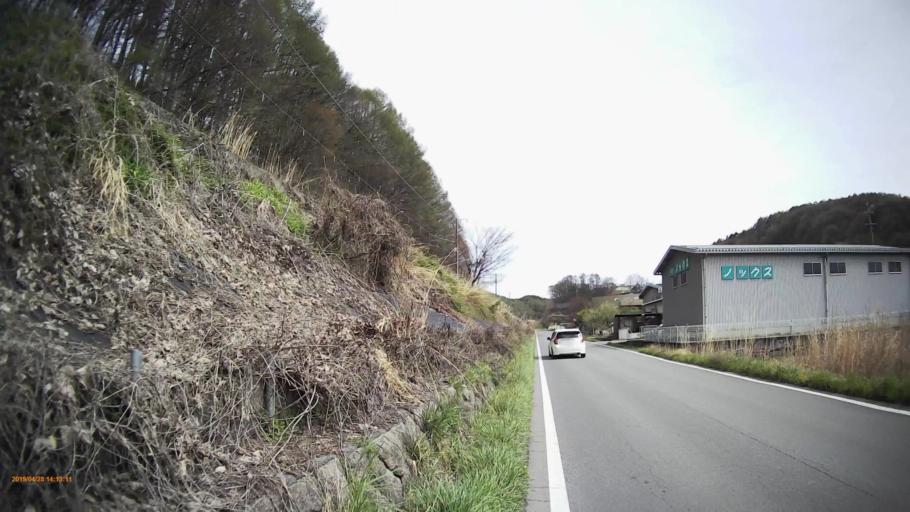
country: JP
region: Nagano
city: Chino
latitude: 35.9785
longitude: 138.1684
